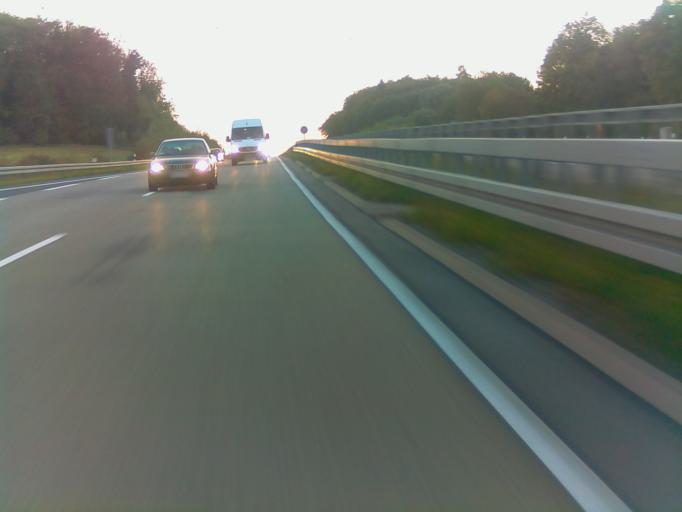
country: DE
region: Hesse
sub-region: Regierungsbezirk Giessen
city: Lich
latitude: 50.5439
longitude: 8.7811
